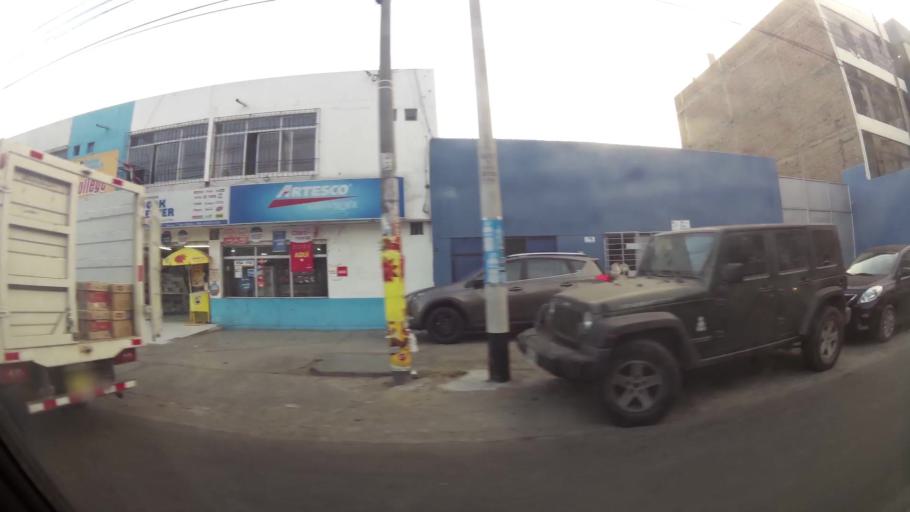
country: PE
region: La Libertad
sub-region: Provincia de Trujillo
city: Trujillo
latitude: -8.1020
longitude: -79.0348
